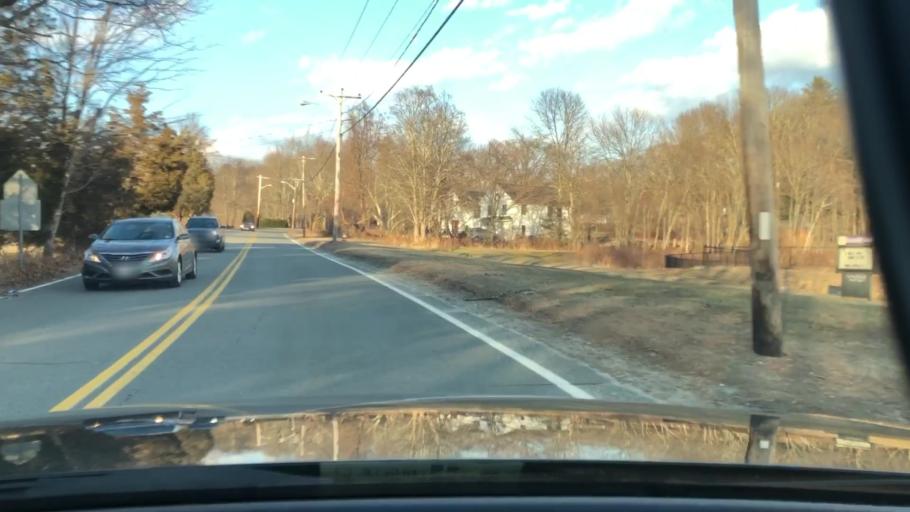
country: US
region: Massachusetts
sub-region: Worcester County
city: Blackstone
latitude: 42.0318
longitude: -71.5392
